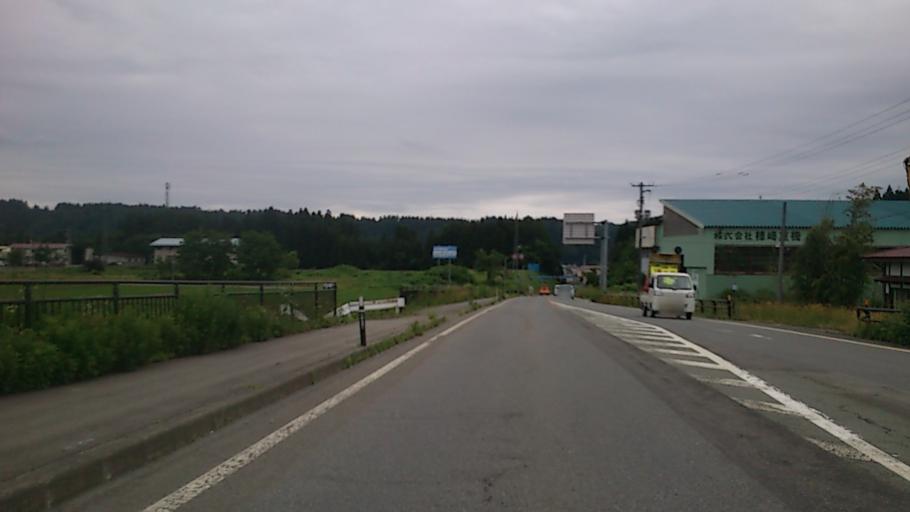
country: JP
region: Yamagata
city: Shinjo
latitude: 38.7020
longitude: 140.3193
